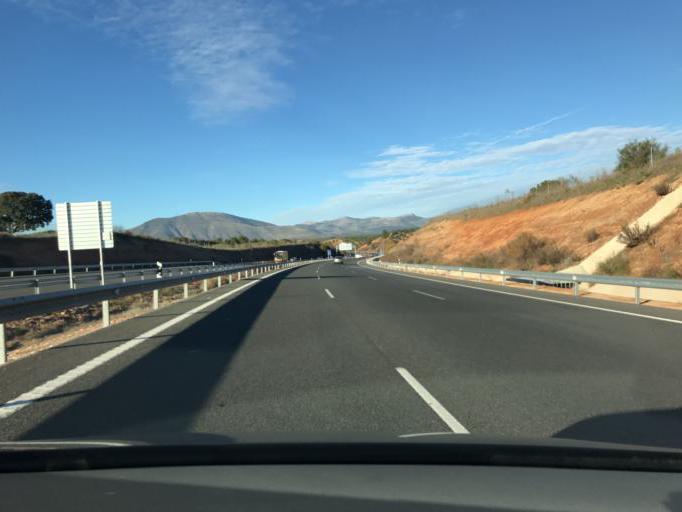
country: ES
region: Andalusia
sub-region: Provincia de Granada
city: Calicasas
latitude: 37.2768
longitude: -3.6585
